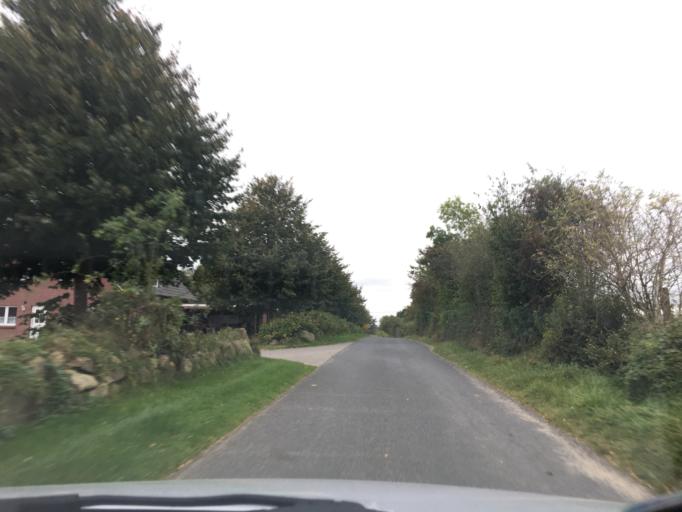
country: DE
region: Schleswig-Holstein
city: Melsdorf
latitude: 54.3203
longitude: 10.0102
